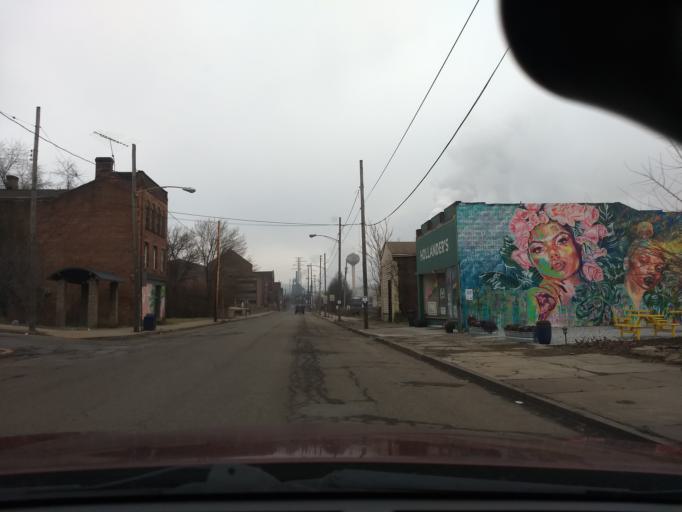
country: US
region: Pennsylvania
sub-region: Allegheny County
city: Braddock
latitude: 40.3999
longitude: -79.8639
